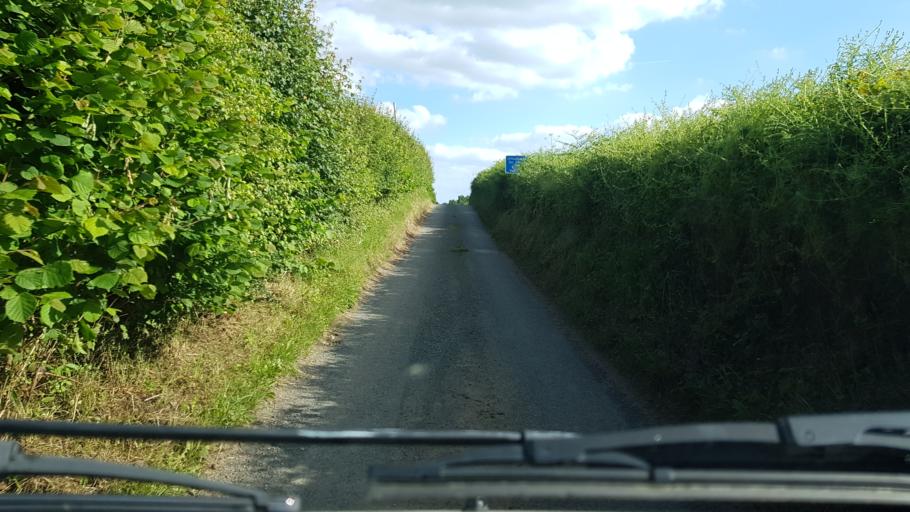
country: GB
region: England
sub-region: Worcestershire
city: Bewdley
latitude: 52.3506
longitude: -2.3315
